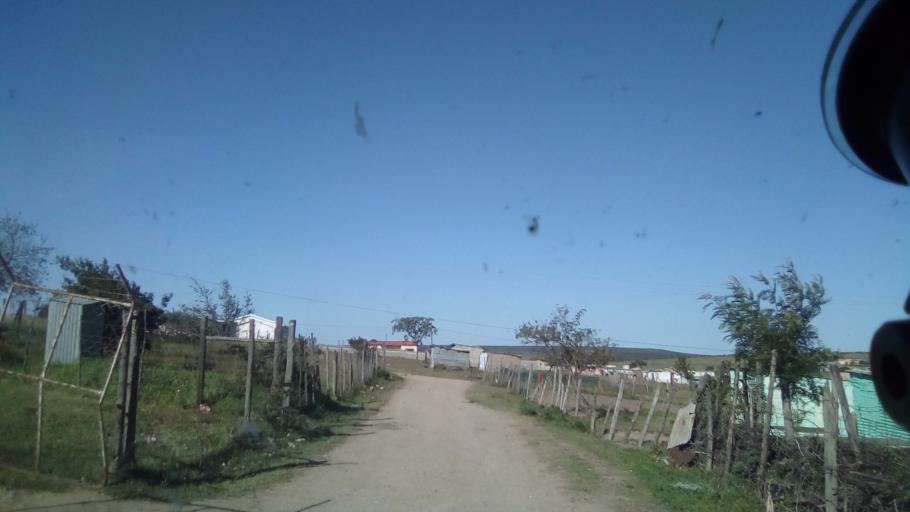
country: ZA
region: Eastern Cape
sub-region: Buffalo City Metropolitan Municipality
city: Bhisho
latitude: -32.8274
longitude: 27.3694
